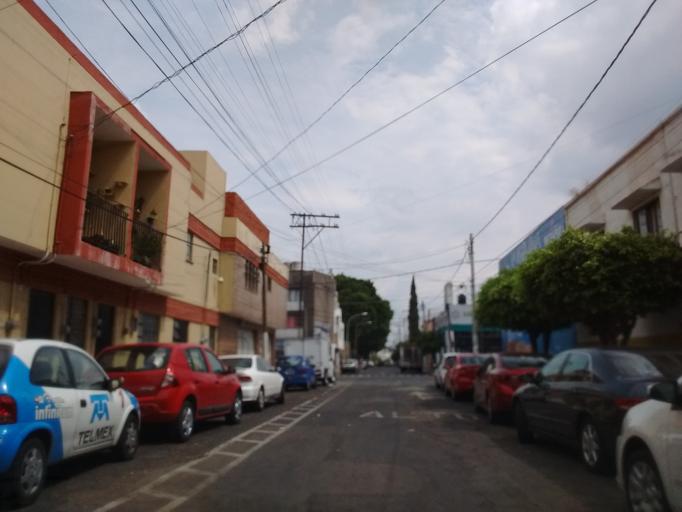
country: MX
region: Jalisco
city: Guadalajara
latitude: 20.6669
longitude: -103.3583
